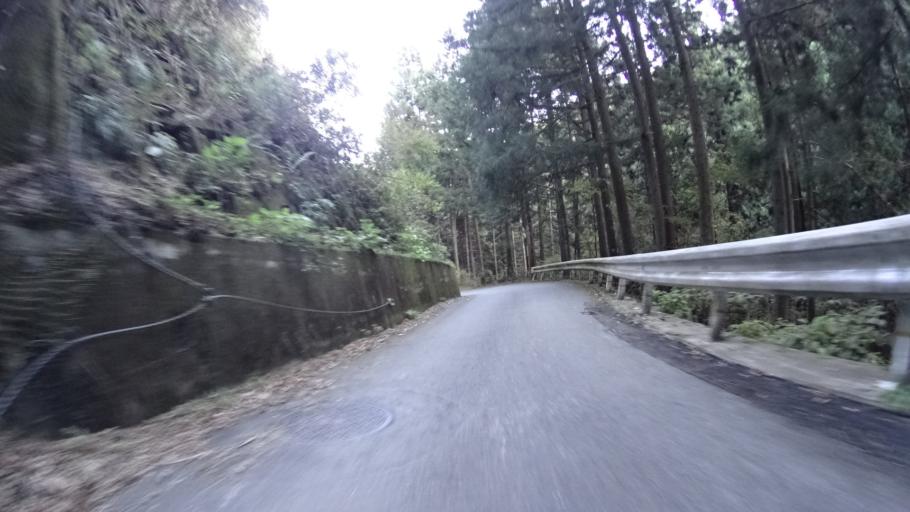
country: JP
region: Yamanashi
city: Uenohara
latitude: 35.6588
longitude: 139.1757
